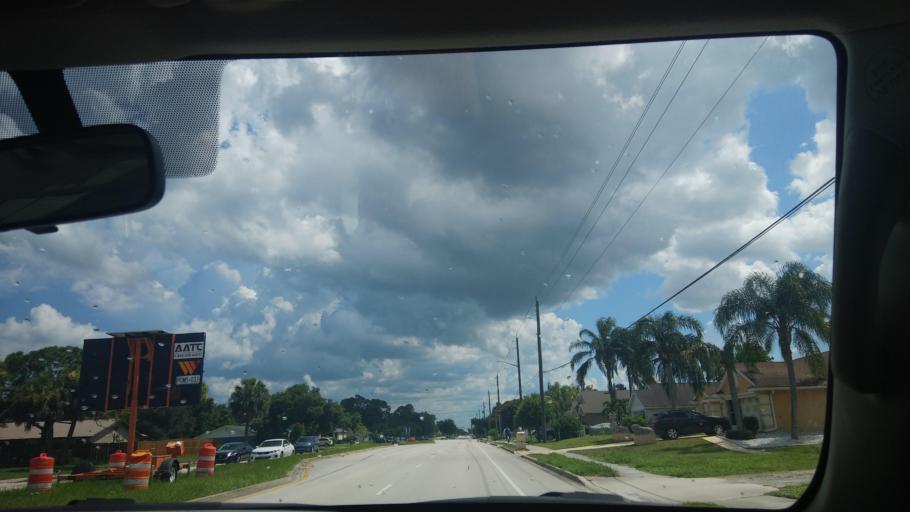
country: US
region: Florida
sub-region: Brevard County
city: Palm Bay
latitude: 27.9928
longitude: -80.6486
